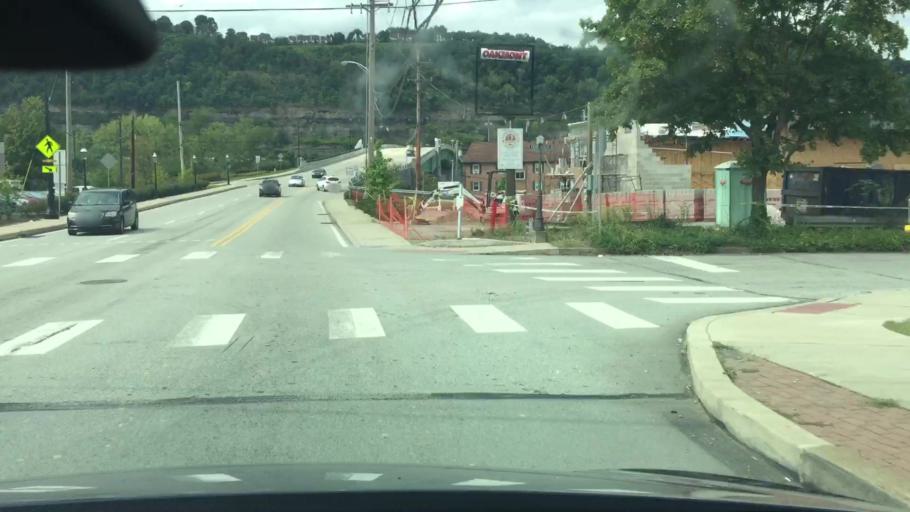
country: US
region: Pennsylvania
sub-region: Allegheny County
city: Oakmont
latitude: 40.5260
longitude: -79.8425
